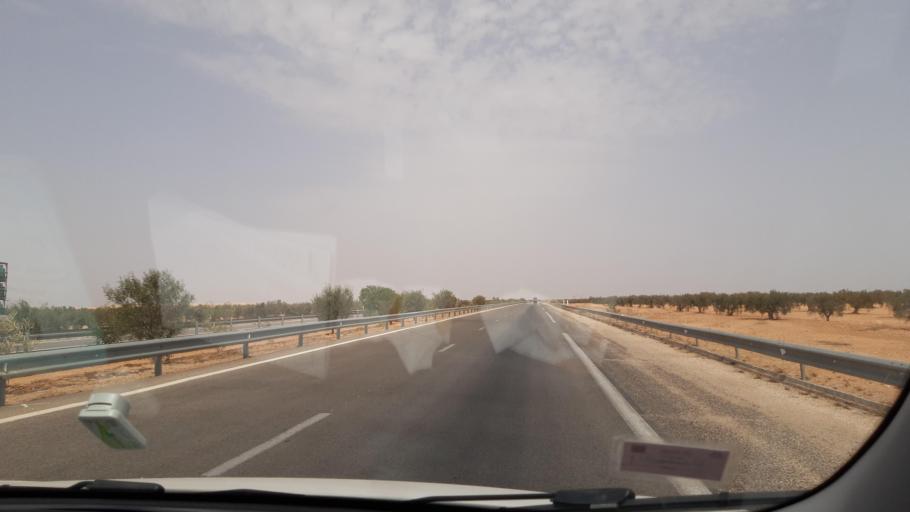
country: TN
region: Safaqis
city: Bi'r `Ali Bin Khalifah
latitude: 34.5547
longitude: 10.3291
